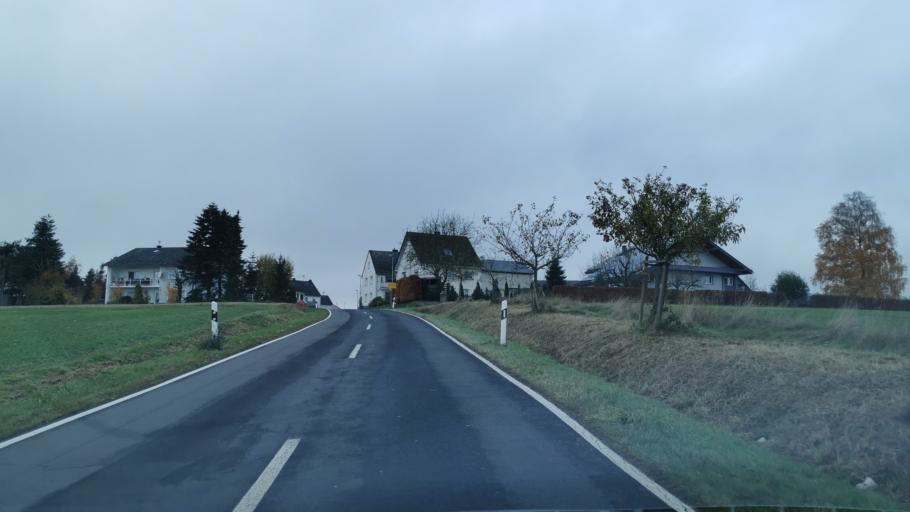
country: DE
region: Rheinland-Pfalz
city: Greimersburg
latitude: 50.1830
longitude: 7.1454
